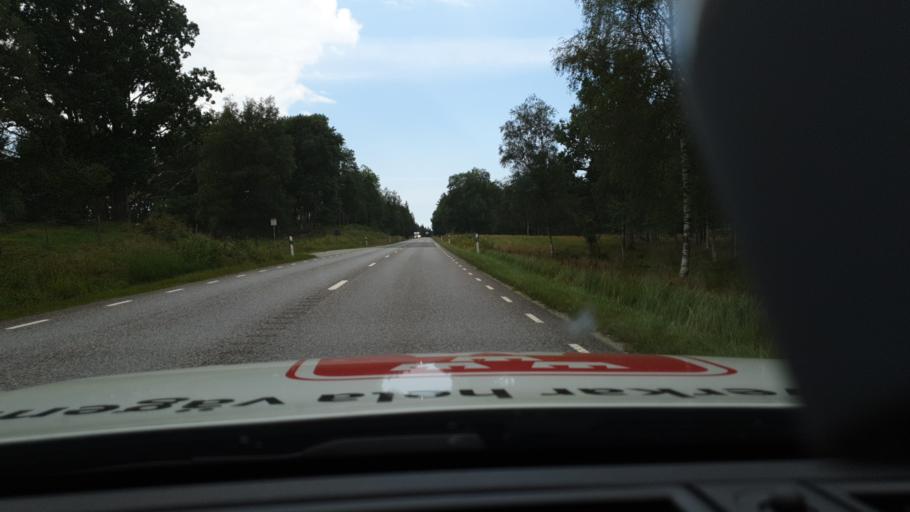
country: SE
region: Joenkoeping
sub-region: Gislaveds Kommun
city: Reftele
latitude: 57.1624
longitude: 13.5582
